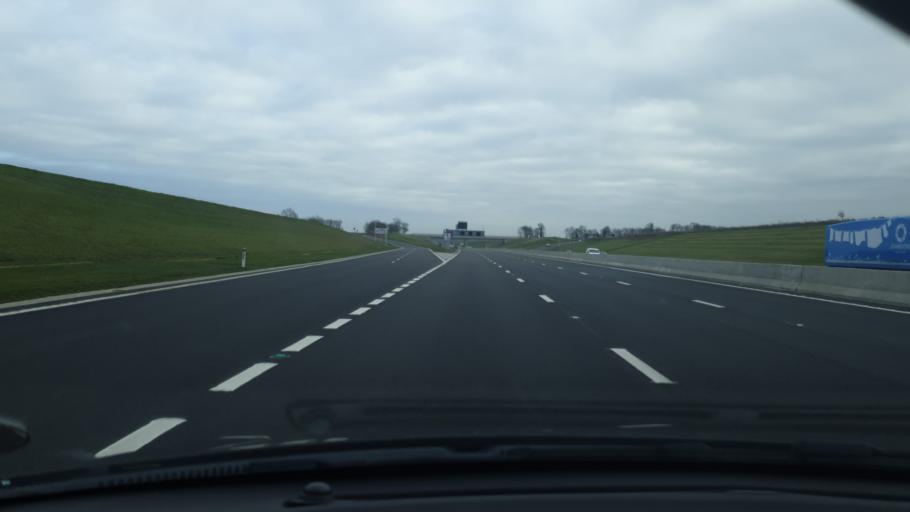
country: GB
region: England
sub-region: Cambridgeshire
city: Godmanchester
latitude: 52.2932
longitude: -0.1572
